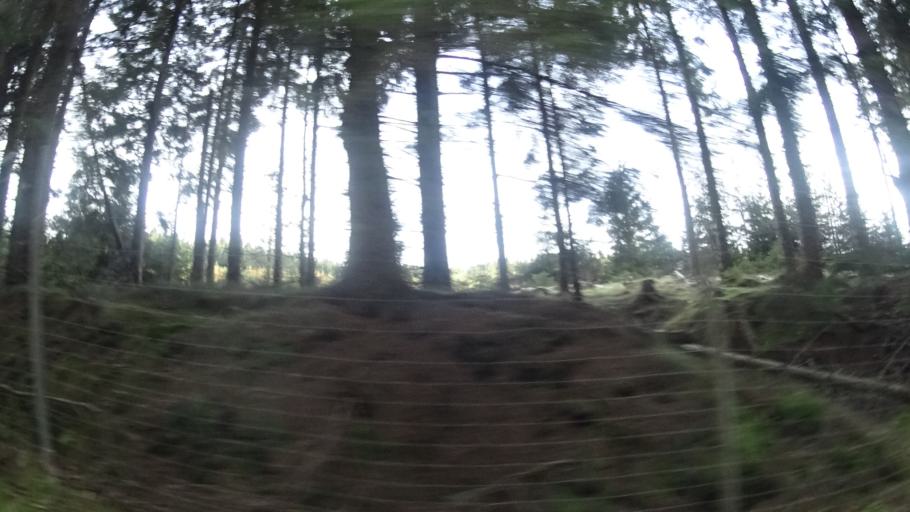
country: DE
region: Thuringia
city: Grafenhain
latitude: 50.8039
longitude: 10.6760
